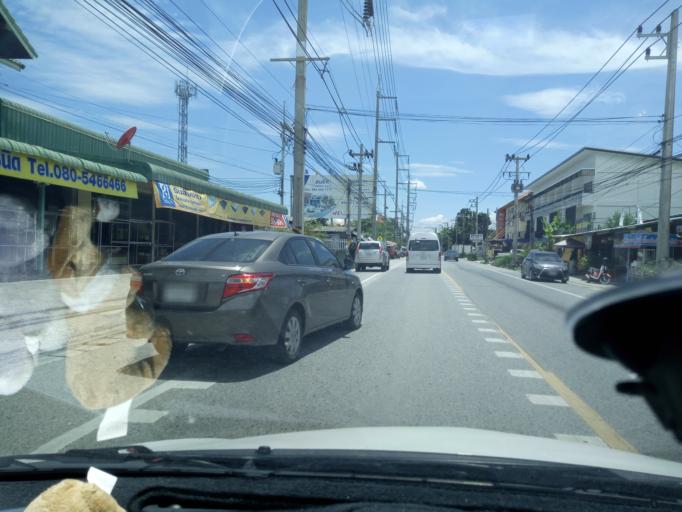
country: TH
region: Chon Buri
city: Phan Thong
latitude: 13.4324
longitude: 101.0622
